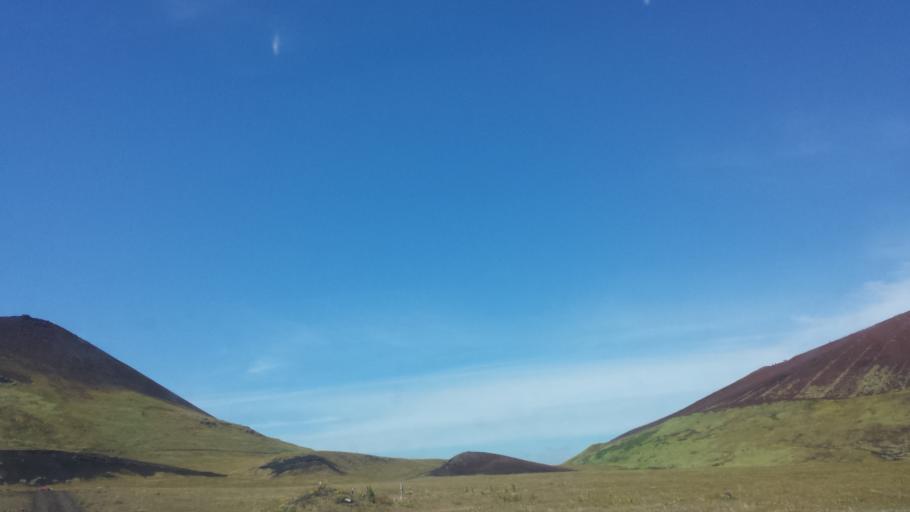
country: IS
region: South
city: Vestmannaeyjar
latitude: 63.4264
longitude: -20.2492
